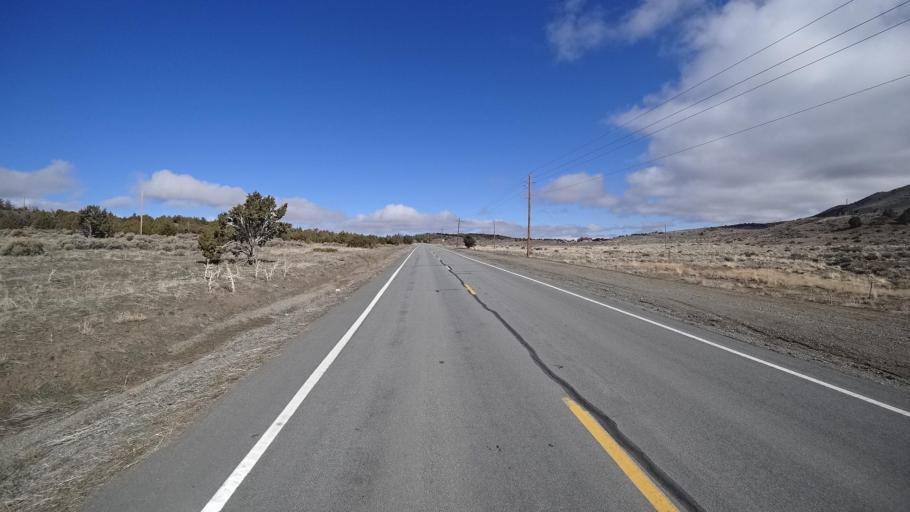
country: US
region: Nevada
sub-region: Washoe County
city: Cold Springs
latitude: 39.7666
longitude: -119.8862
